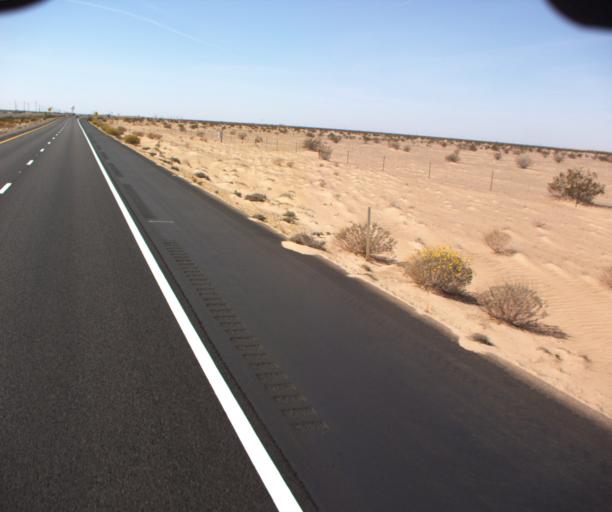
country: US
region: Arizona
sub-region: Yuma County
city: Somerton
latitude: 32.4954
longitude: -114.6351
